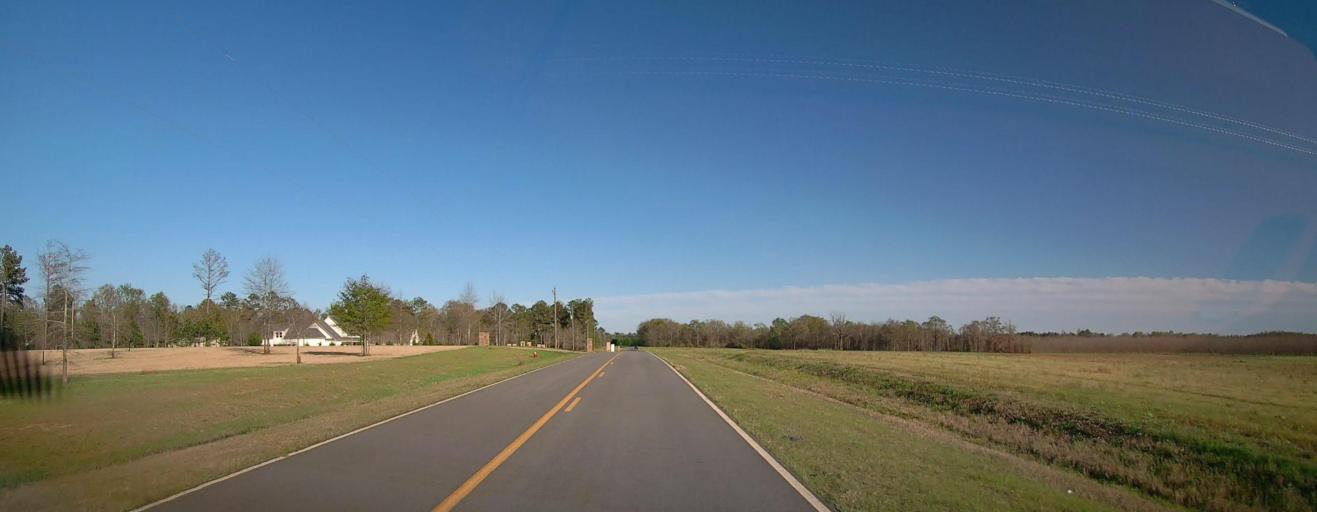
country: US
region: Georgia
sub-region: Dooly County
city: Unadilla
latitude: 32.3503
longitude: -83.6217
